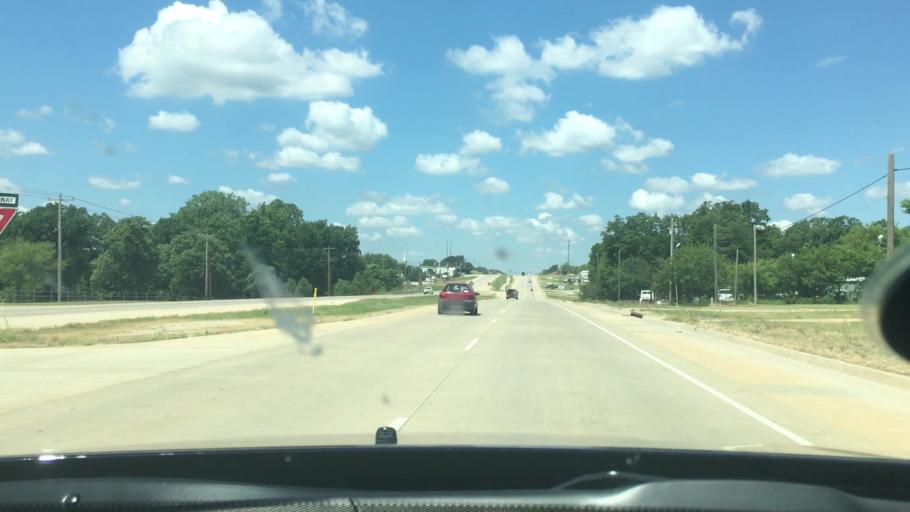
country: US
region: Oklahoma
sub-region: Carter County
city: Lone Grove
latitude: 34.1730
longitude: -97.2323
